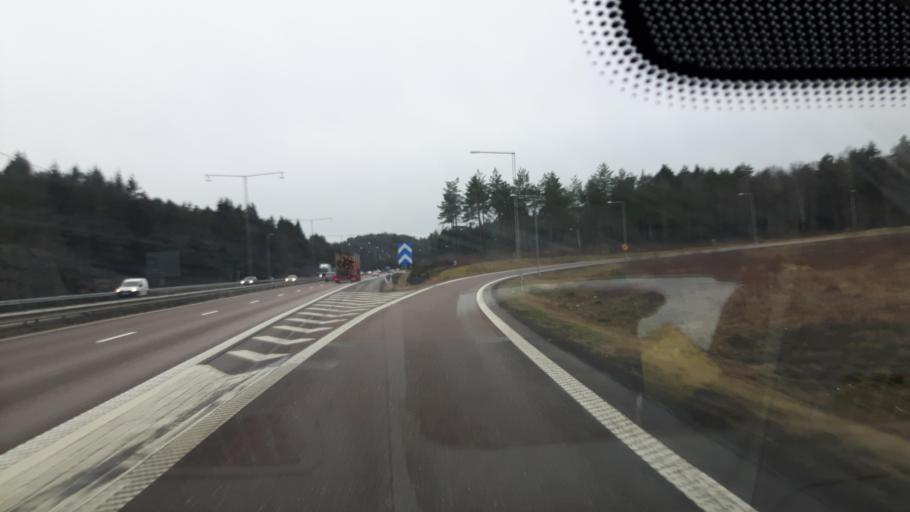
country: SE
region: Vaestra Goetaland
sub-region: Molndal
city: Lindome
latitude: 57.5713
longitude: 12.0577
